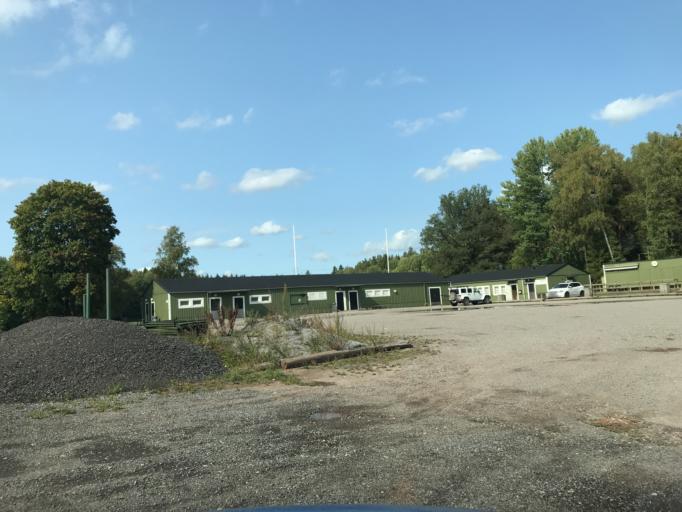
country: SE
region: Stockholm
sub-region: Sollentuna Kommun
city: Sollentuna
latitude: 59.4496
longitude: 17.9696
